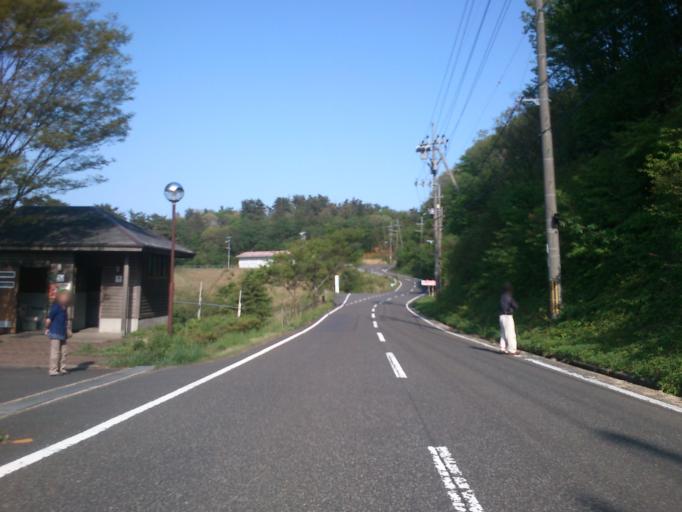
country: JP
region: Kyoto
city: Miyazu
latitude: 35.7183
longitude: 135.1913
